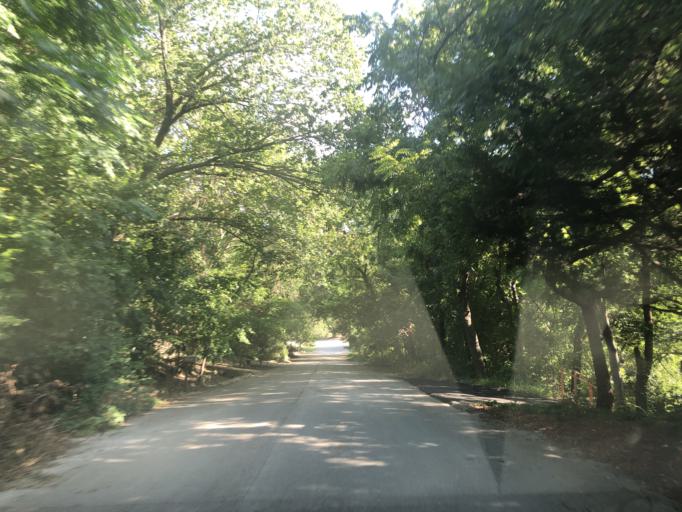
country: US
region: Texas
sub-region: Dallas County
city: Duncanville
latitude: 32.6667
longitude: -96.9233
